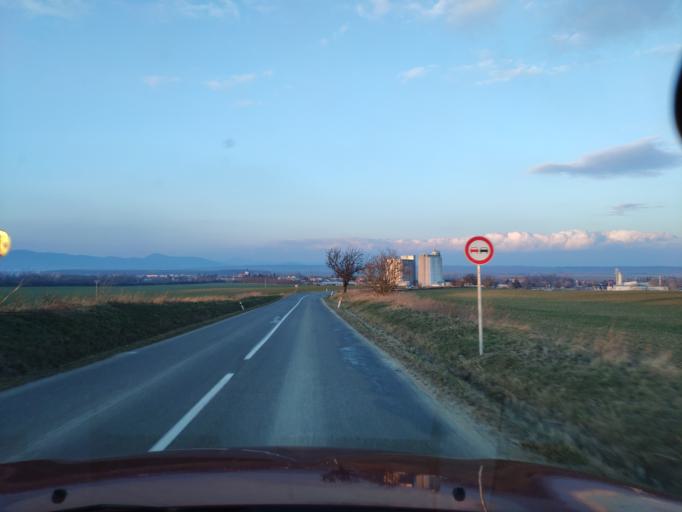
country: SK
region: Nitriansky
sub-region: Okres Nitra
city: Nitra
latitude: 48.2319
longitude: 18.1064
